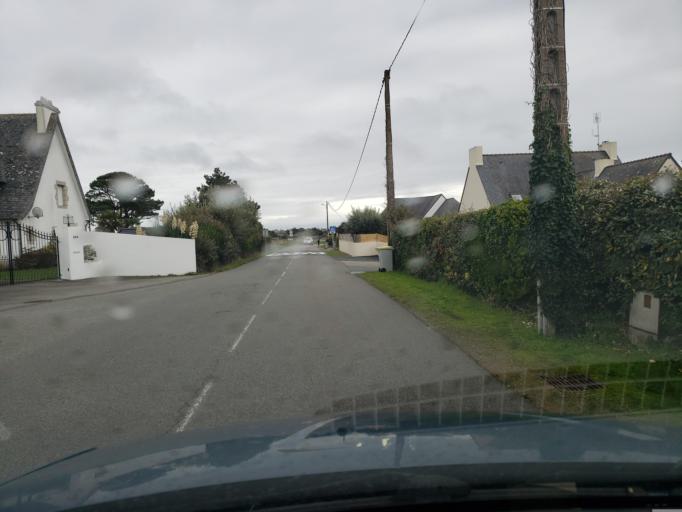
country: FR
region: Brittany
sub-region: Departement du Finistere
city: Guilvinec
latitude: 47.8054
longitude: -4.3044
